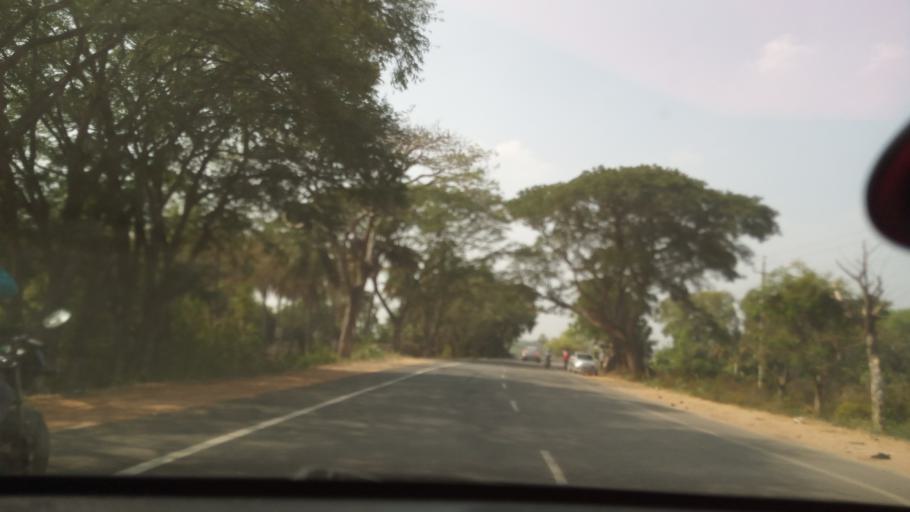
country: IN
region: Karnataka
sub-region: Mysore
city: Nanjangud
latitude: 12.1056
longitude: 76.7082
